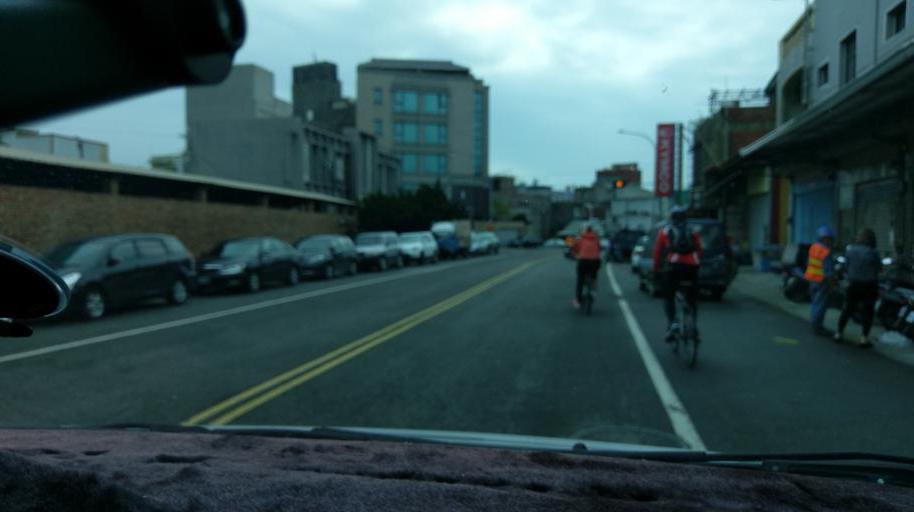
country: TW
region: Taiwan
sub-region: Miaoli
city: Miaoli
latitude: 24.4927
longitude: 120.6798
